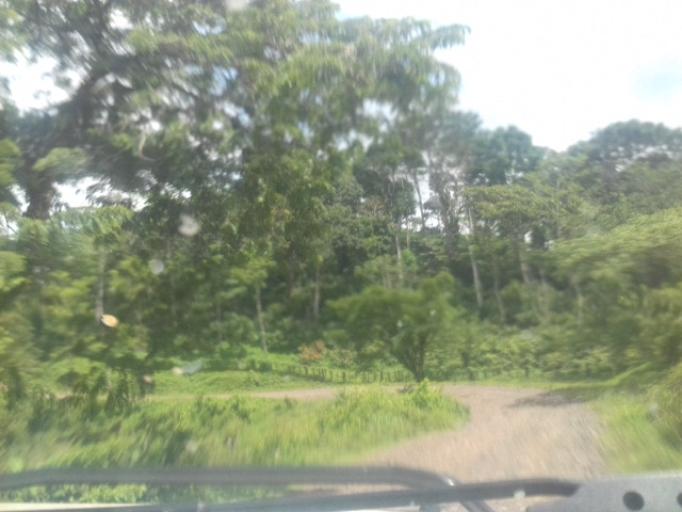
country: NI
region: Matagalpa
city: Matiguas
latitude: 12.9324
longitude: -85.3667
